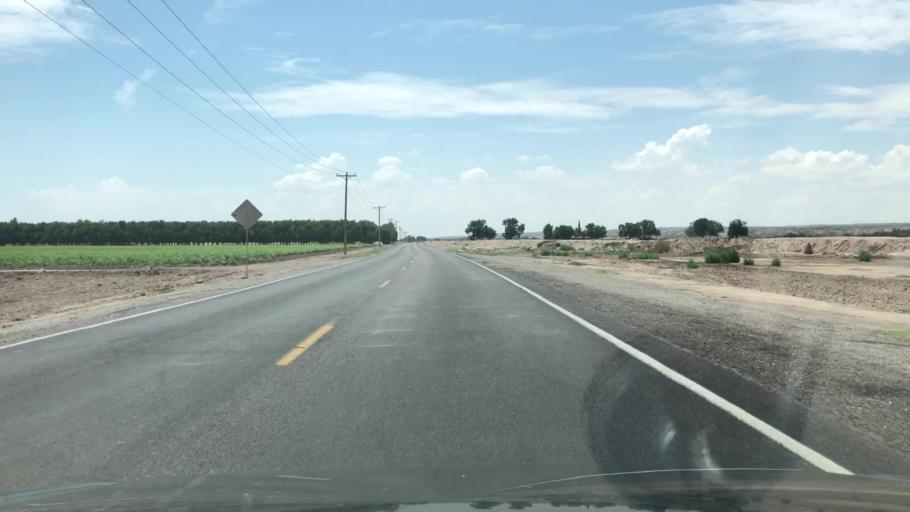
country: US
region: New Mexico
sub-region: Dona Ana County
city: Vado
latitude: 32.0806
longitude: -106.6836
